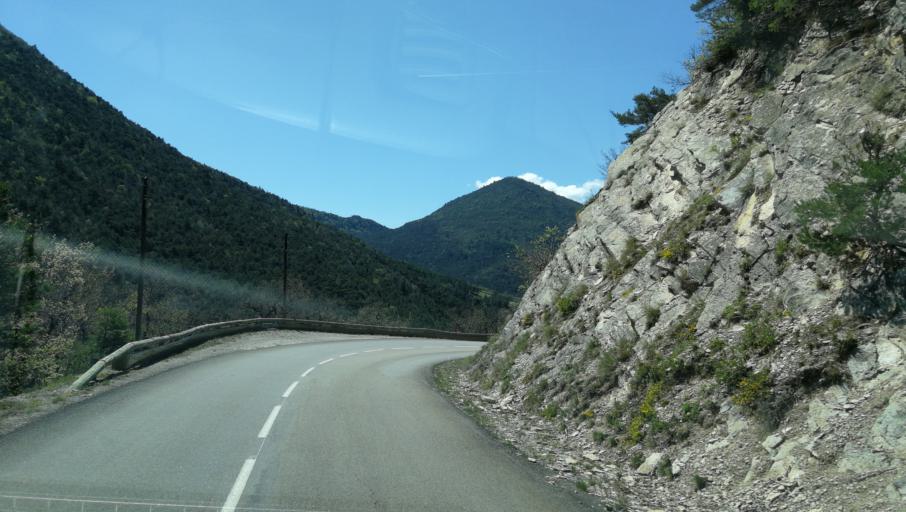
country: FR
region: Rhone-Alpes
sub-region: Departement de la Drome
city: Die
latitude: 44.8073
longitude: 5.3931
